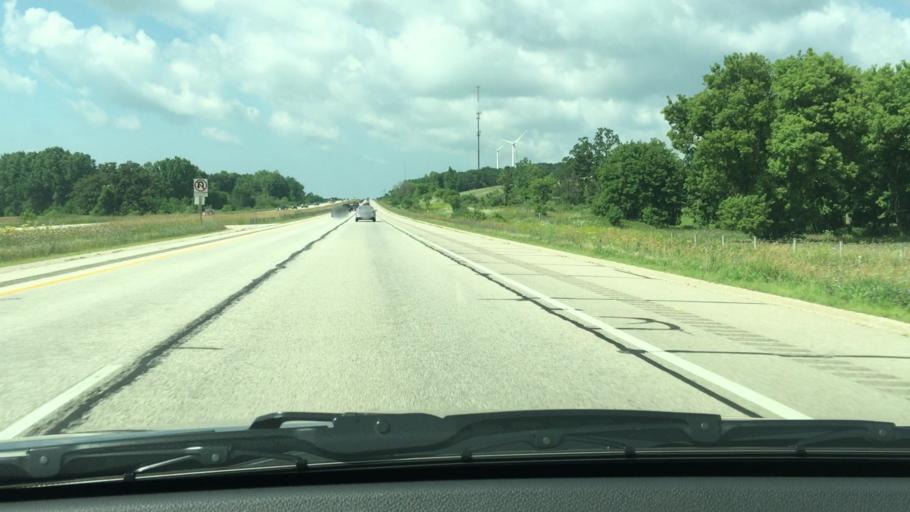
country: US
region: Wisconsin
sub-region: Dodge County
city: Lomira
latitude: 43.6466
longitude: -88.4414
